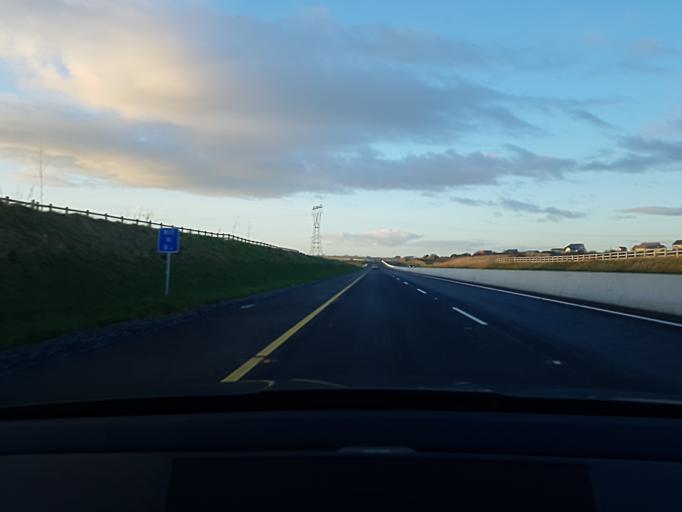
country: IE
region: Connaught
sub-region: County Galway
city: Athenry
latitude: 53.3784
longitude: -8.7966
